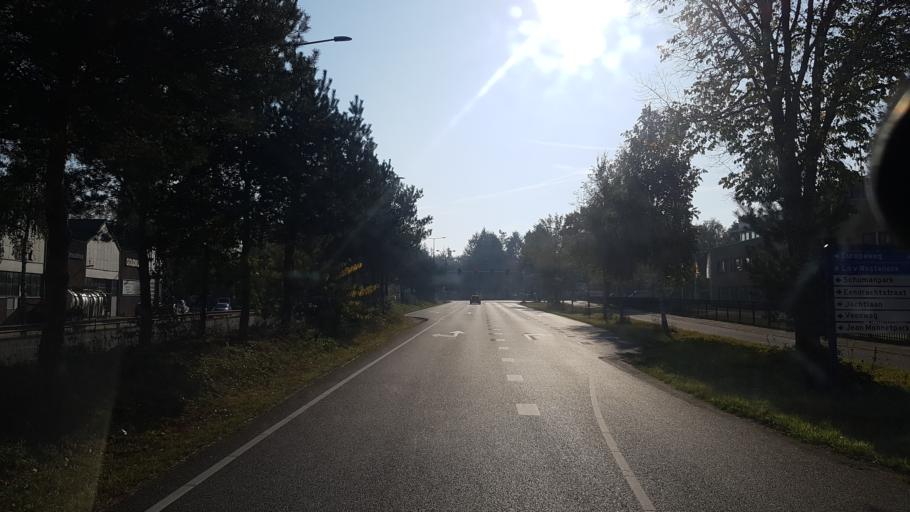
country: NL
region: Gelderland
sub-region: Gemeente Apeldoorn
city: Apeldoorn
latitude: 52.1946
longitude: 5.9350
